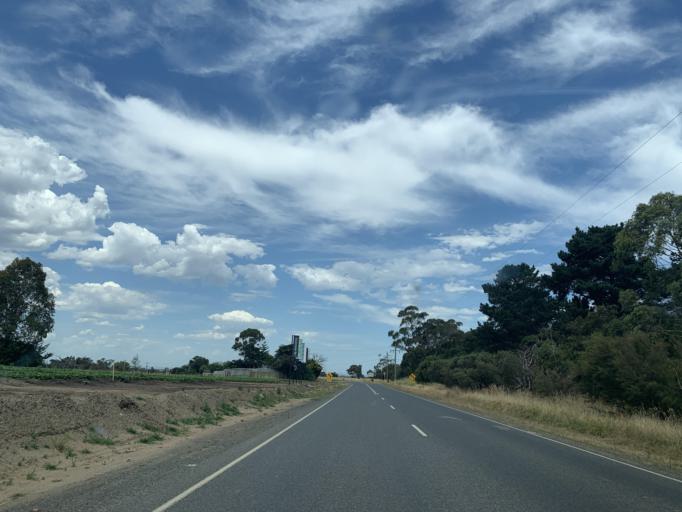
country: AU
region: Victoria
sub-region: Casey
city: Junction Village
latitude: -38.1334
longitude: 145.3328
